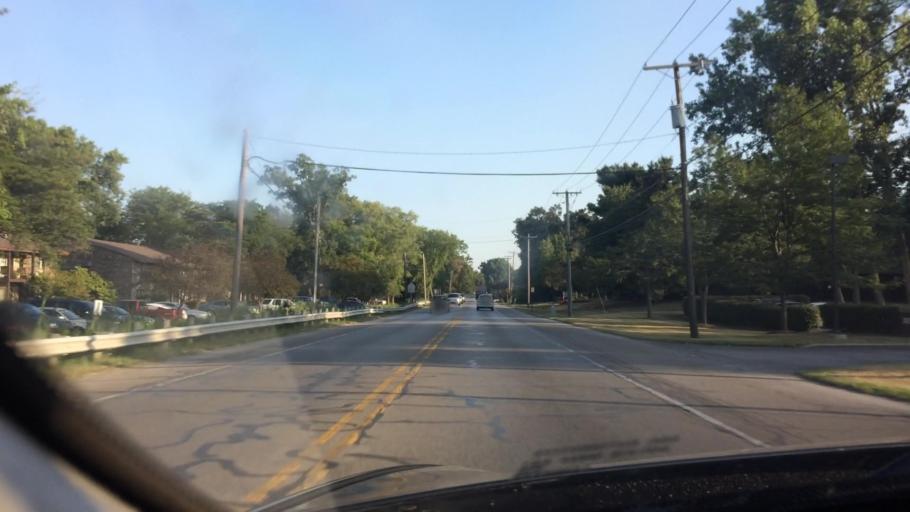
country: US
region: Ohio
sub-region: Lucas County
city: Holland
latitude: 41.6588
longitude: -83.7022
